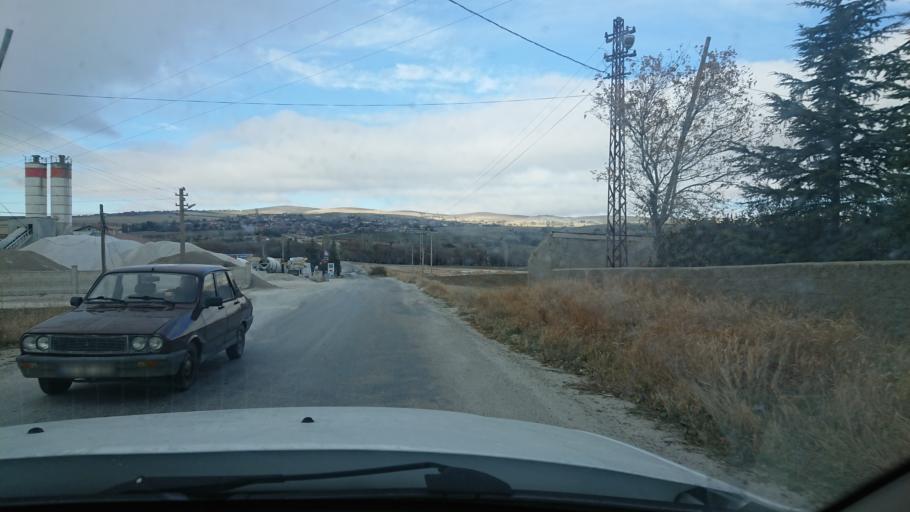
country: TR
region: Aksaray
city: Ortakoy
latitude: 38.7508
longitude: 34.0244
